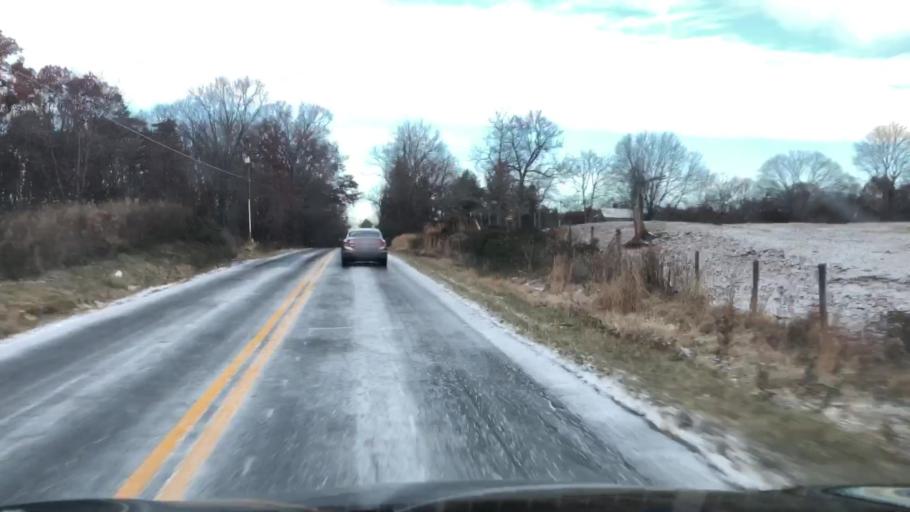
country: US
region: Virginia
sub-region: Prince William County
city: Nokesville
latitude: 38.6855
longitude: -77.6681
